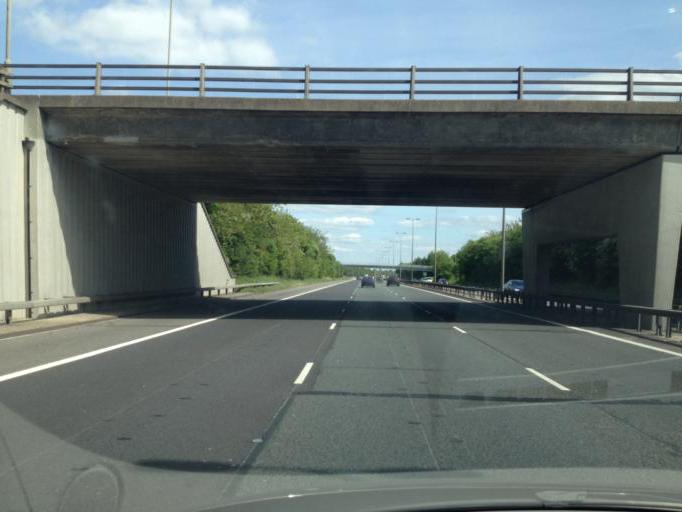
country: GB
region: England
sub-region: Buckinghamshire
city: Stokenchurch
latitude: 51.6609
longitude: -0.9135
